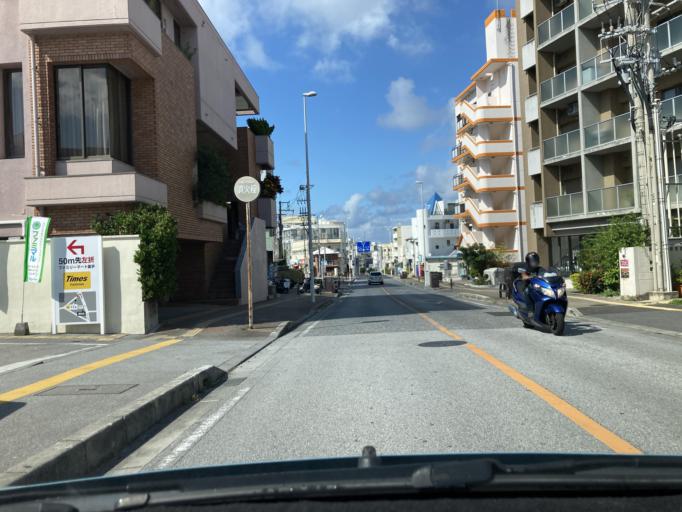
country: JP
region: Okinawa
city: Naha-shi
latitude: 26.2128
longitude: 127.6854
